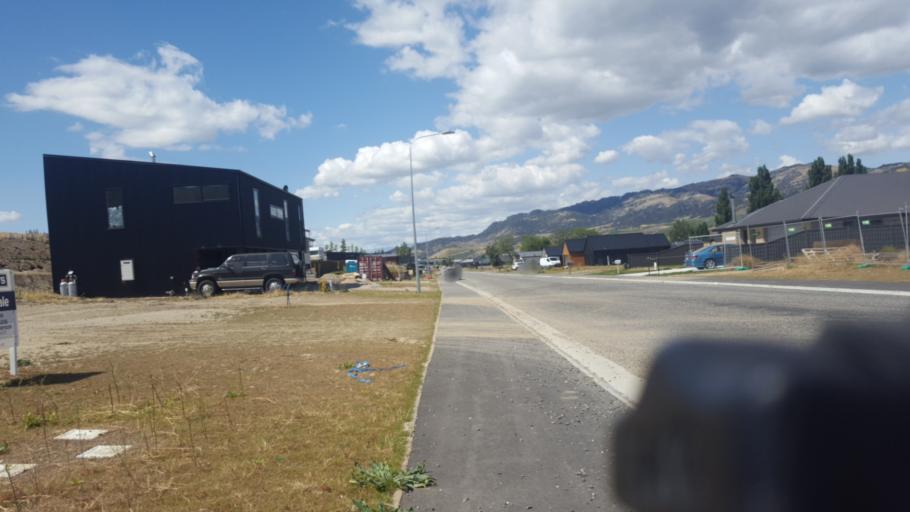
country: NZ
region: Otago
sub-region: Queenstown-Lakes District
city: Wanaka
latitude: -44.9758
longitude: 169.2384
